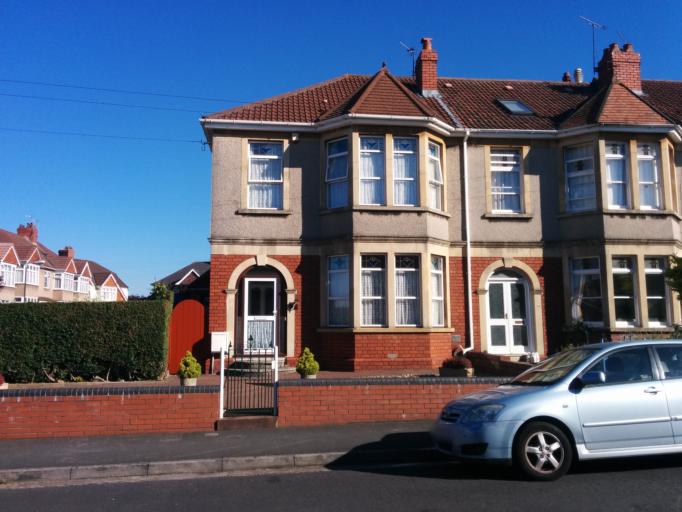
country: GB
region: England
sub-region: Bristol
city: Bristol
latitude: 51.4361
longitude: -2.5746
